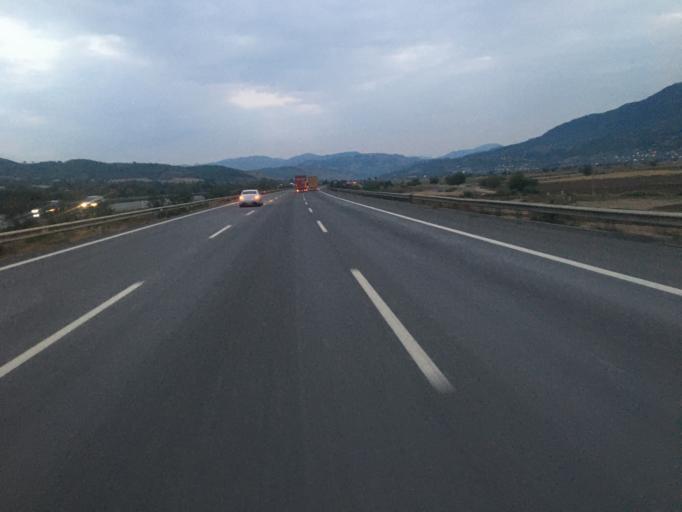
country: TR
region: Osmaniye
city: Osmaniye
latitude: 37.1408
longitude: 36.3205
